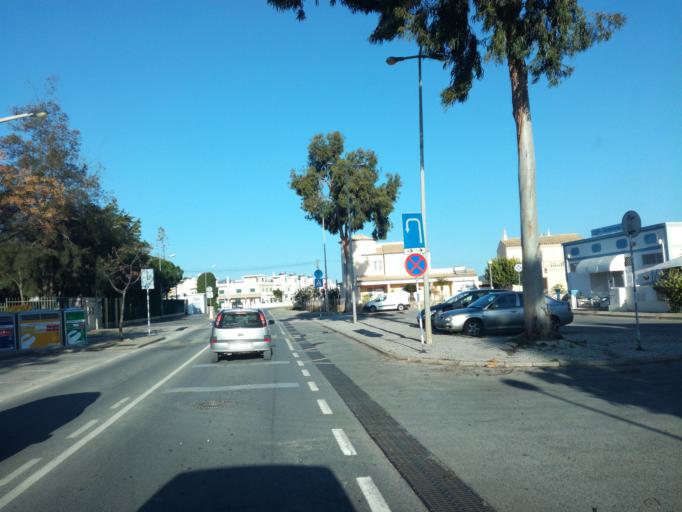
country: PT
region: Faro
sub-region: Olhao
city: Laranjeiro
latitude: 37.0570
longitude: -7.7613
